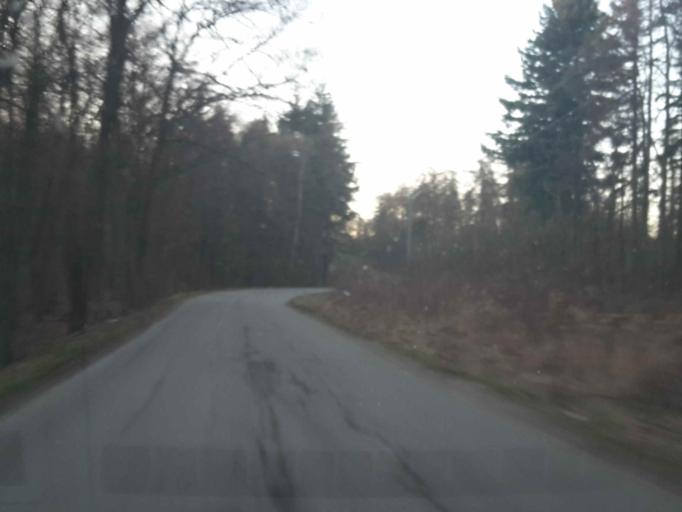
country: CZ
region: South Moravian
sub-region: Okres Blansko
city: Adamov
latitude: 49.2887
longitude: 16.6403
